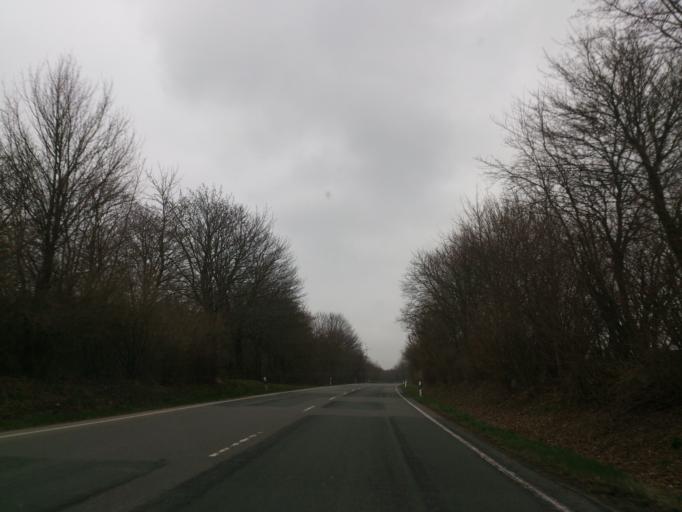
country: DE
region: North Rhine-Westphalia
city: Lichtenau
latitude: 51.5547
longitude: 8.8385
